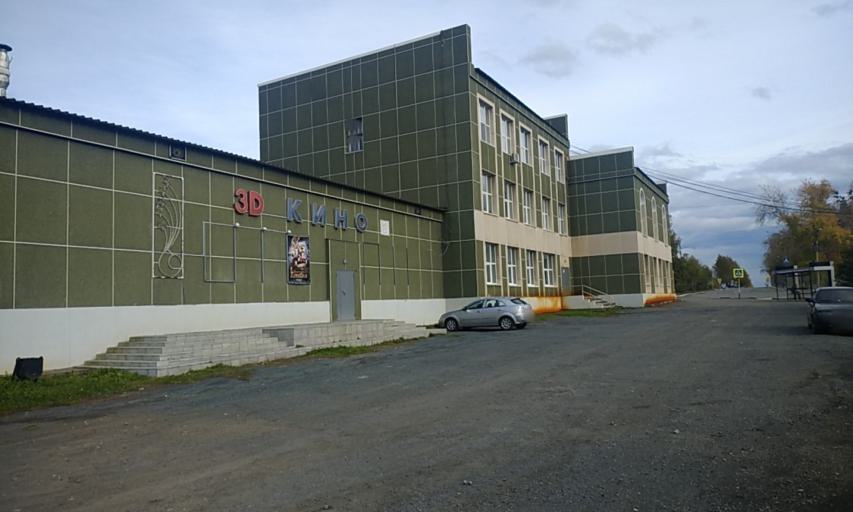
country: RU
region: Sverdlovsk
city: Krasnoural'sk
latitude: 58.3542
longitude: 60.0540
